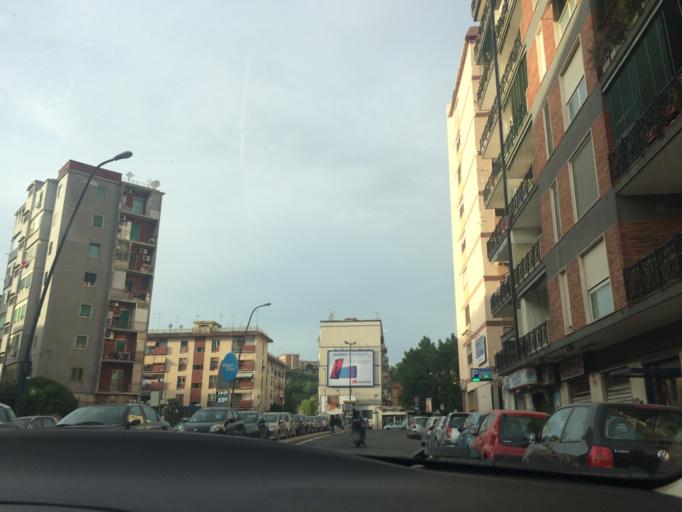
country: IT
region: Campania
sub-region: Provincia di Napoli
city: Bagnoli
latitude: 40.8289
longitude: 14.1961
